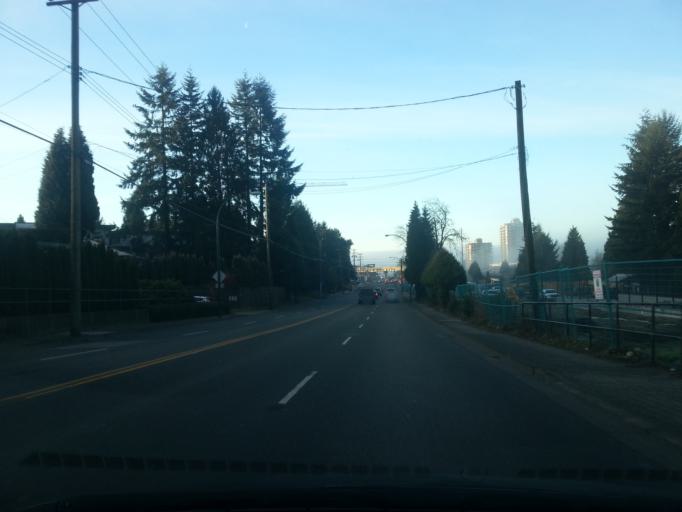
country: CA
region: British Columbia
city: Port Moody
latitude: 49.2655
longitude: -122.8852
